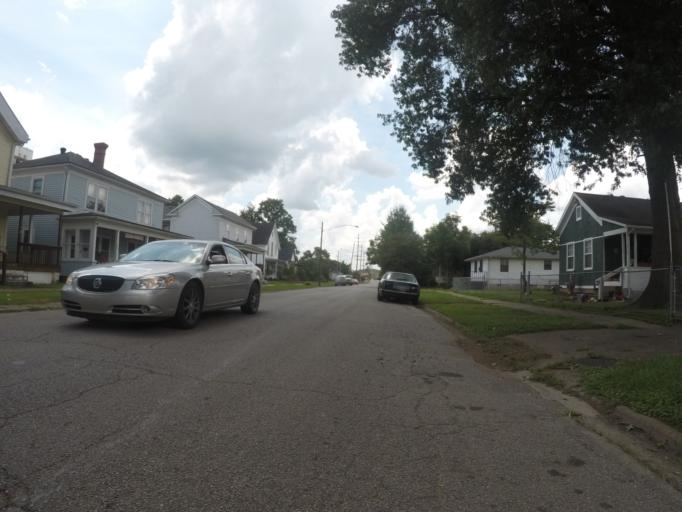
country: US
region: West Virginia
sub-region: Cabell County
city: Huntington
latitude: 38.4286
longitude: -82.3861
